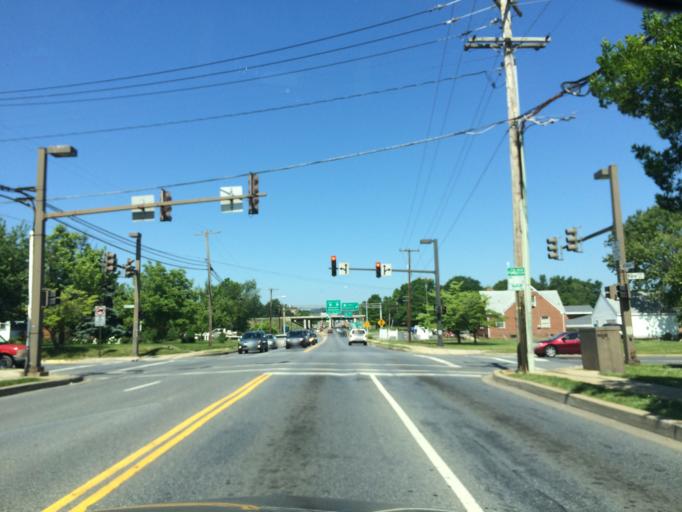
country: US
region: Maryland
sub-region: Frederick County
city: Frederick
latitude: 39.4145
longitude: -77.4305
